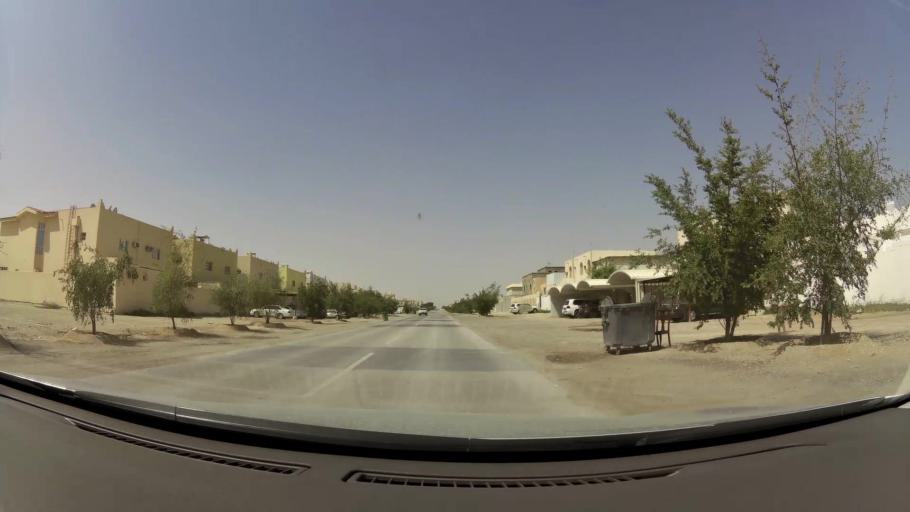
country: QA
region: Baladiyat Umm Salal
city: Umm Salal Muhammad
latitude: 25.3755
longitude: 51.4207
